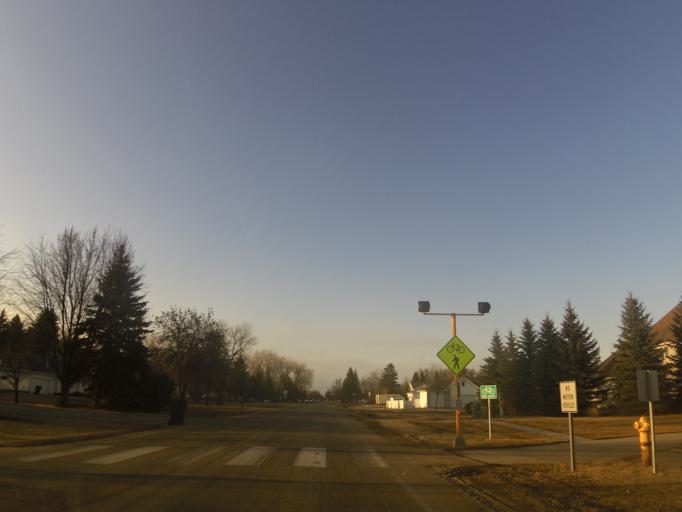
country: US
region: North Dakota
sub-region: Grand Forks County
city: Grand Forks
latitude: 47.8704
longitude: -97.0291
